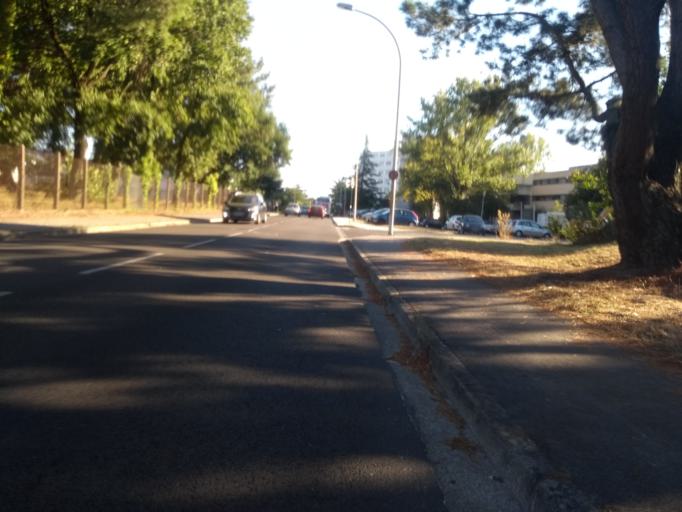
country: FR
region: Aquitaine
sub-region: Departement de la Gironde
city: Gradignan
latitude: 44.7925
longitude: -0.6133
